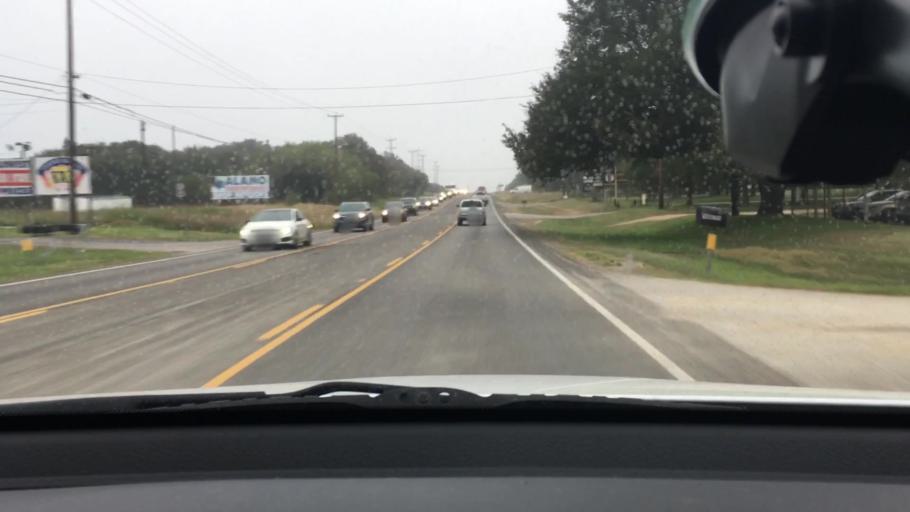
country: US
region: Texas
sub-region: Comal County
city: Garden Ridge
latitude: 29.6155
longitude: -98.3148
